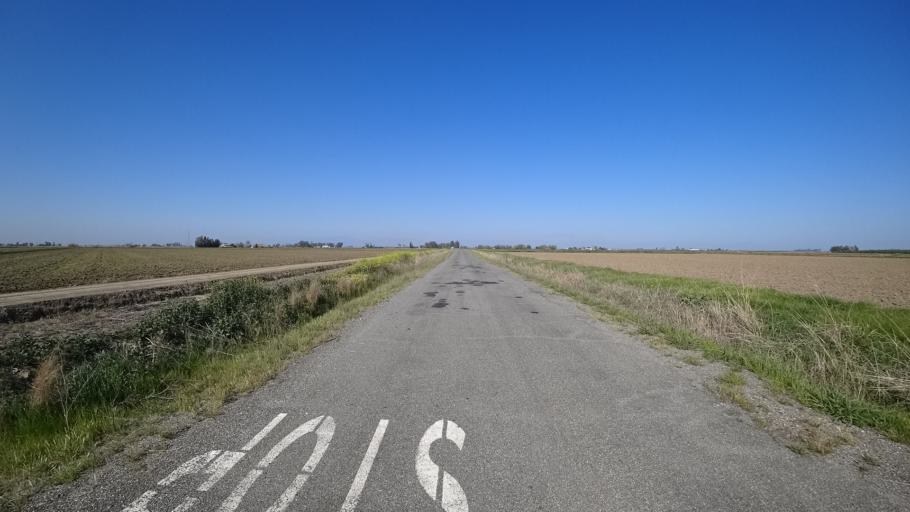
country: US
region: California
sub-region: Glenn County
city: Hamilton City
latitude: 39.6016
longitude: -122.0388
